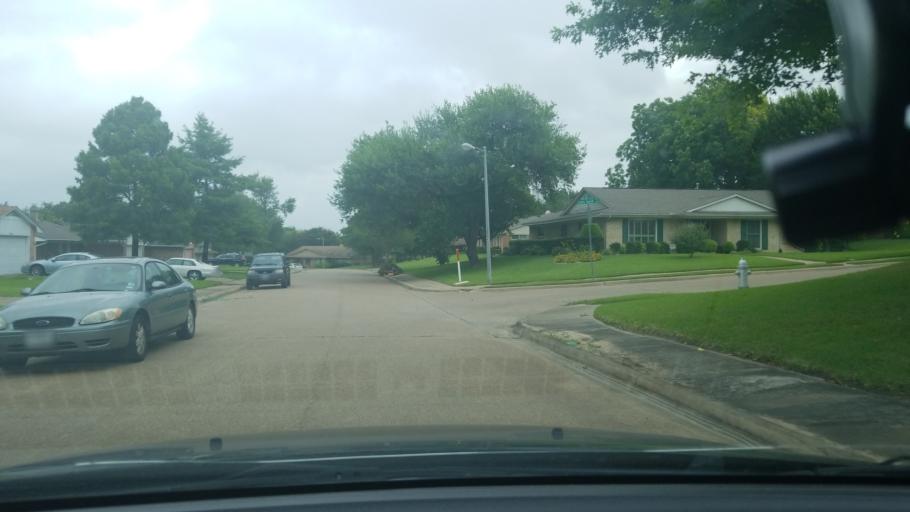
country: US
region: Texas
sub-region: Dallas County
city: Mesquite
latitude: 32.7815
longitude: -96.6342
